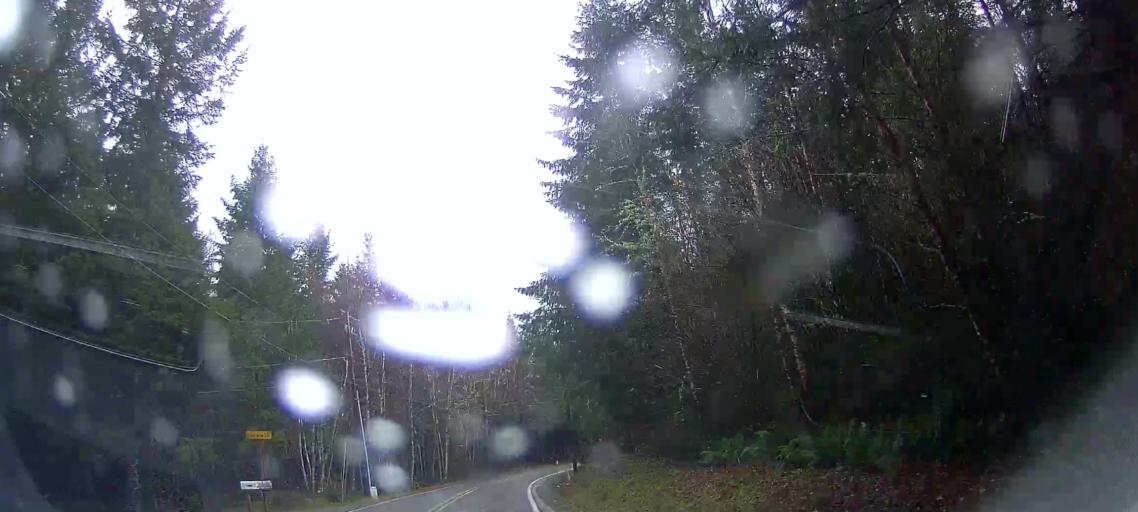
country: US
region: Washington
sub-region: Skagit County
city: Clear Lake
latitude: 48.4769
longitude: -122.1497
